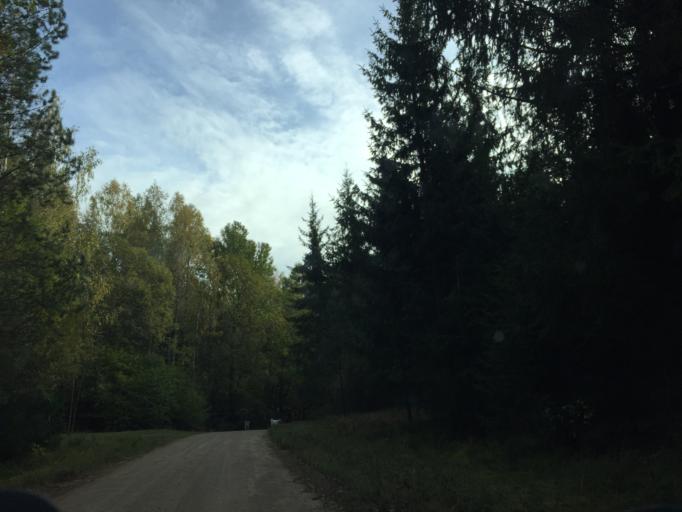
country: LV
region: Jaunpils
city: Jaunpils
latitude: 56.5872
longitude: 23.0112
